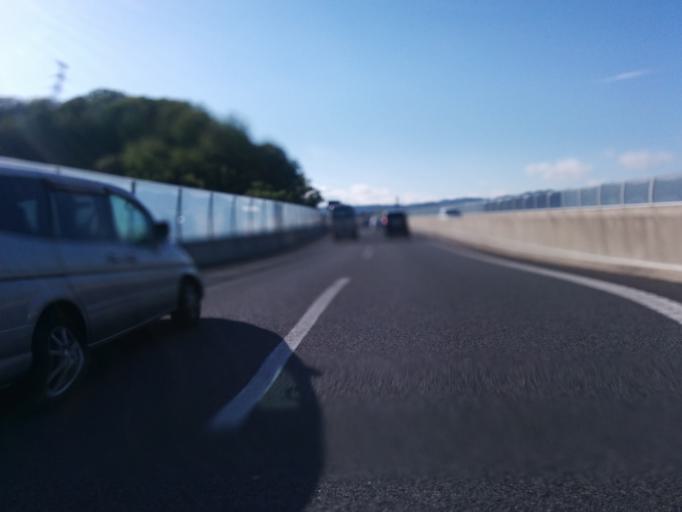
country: JP
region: Shiga Prefecture
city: Kusatsu
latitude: 34.9662
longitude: 135.9625
